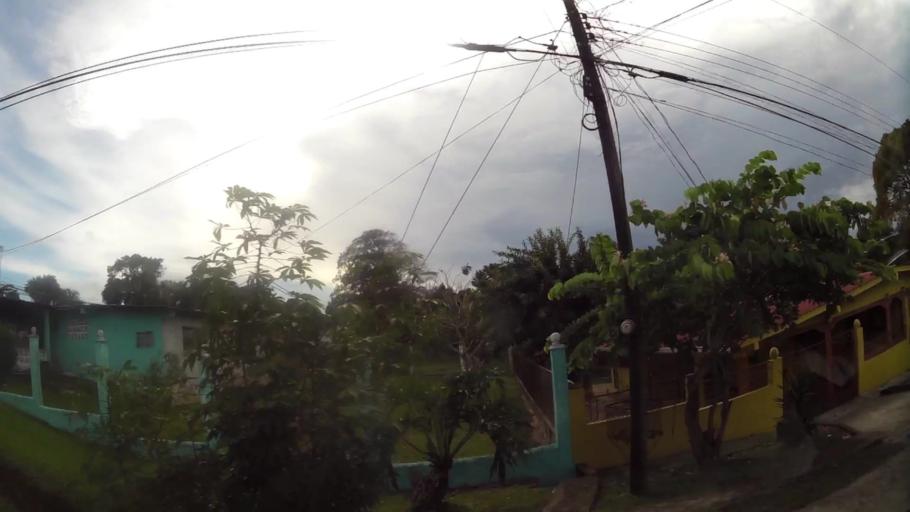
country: PA
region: Panama
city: El Coco
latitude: 8.8706
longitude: -79.8041
